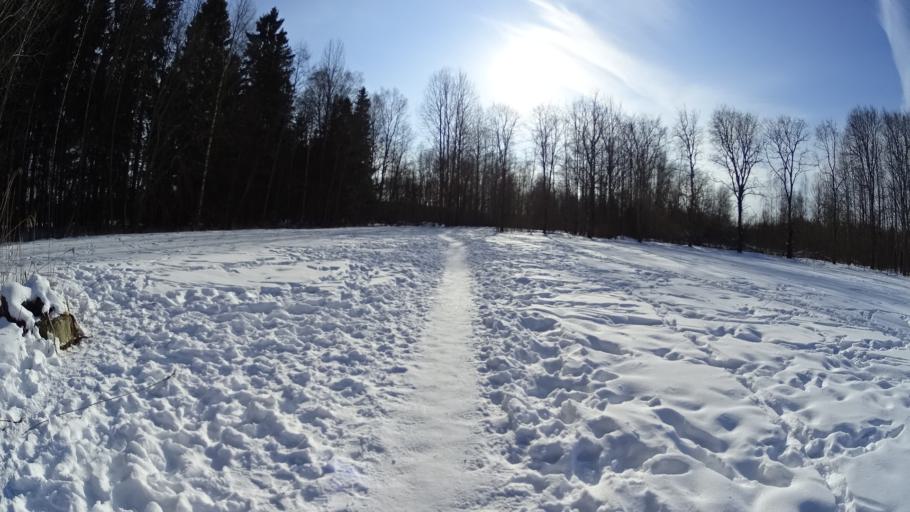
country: FI
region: Uusimaa
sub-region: Helsinki
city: Kauniainen
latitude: 60.2446
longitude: 24.7287
